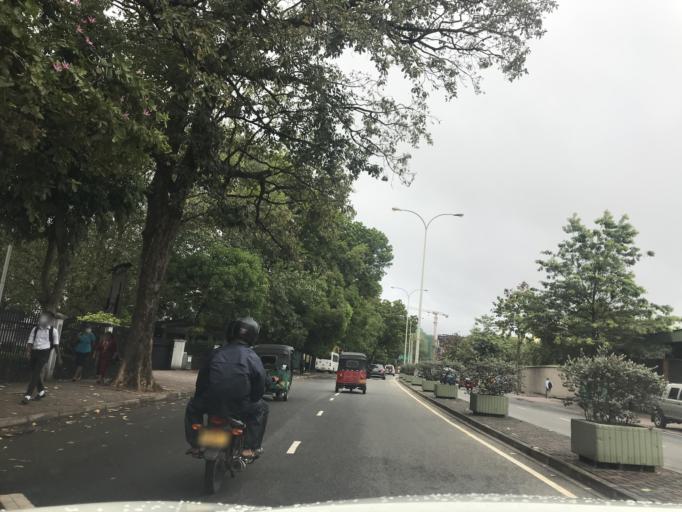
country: LK
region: Western
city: Colombo
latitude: 6.9209
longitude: 79.8644
